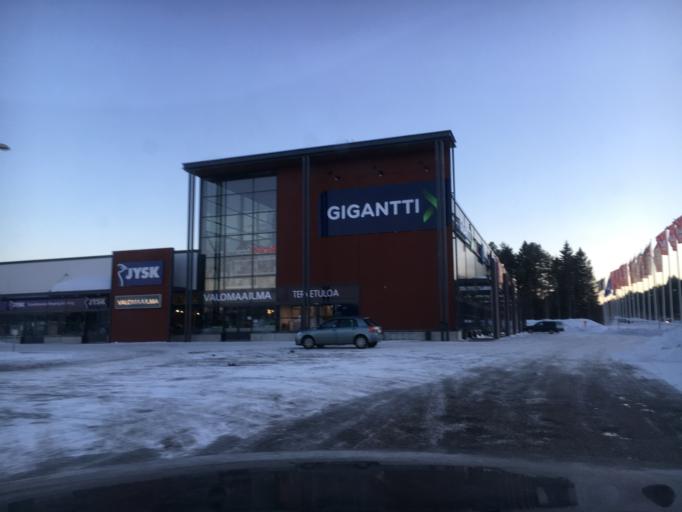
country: FI
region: Kainuu
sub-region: Kajaani
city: Kajaani
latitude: 64.2109
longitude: 27.7722
